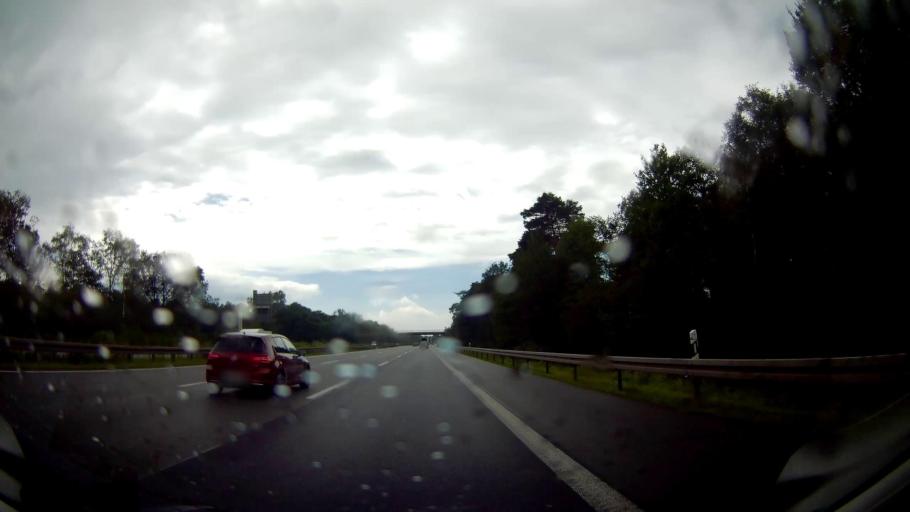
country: DE
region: North Rhine-Westphalia
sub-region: Regierungsbezirk Detmold
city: Guetersloh
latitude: 51.8628
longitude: 8.3607
